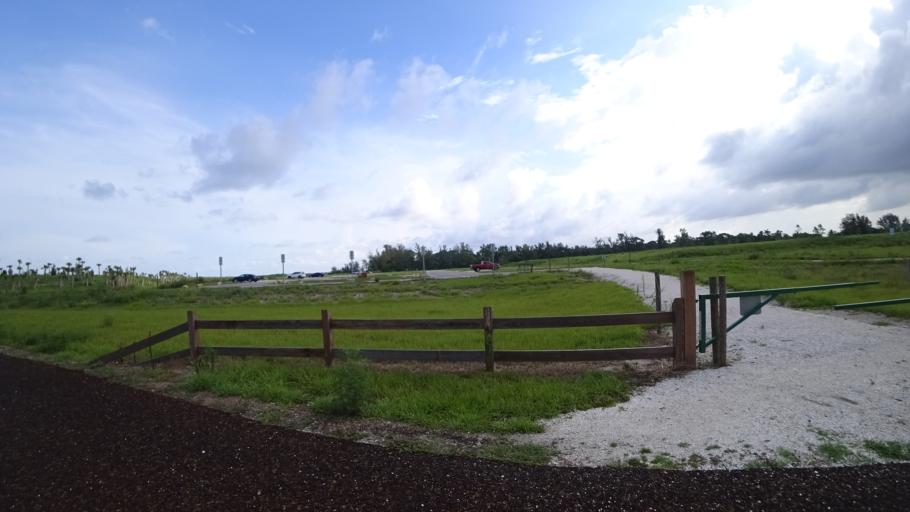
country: US
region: Florida
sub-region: Manatee County
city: Cortez
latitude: 27.5081
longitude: -82.6647
